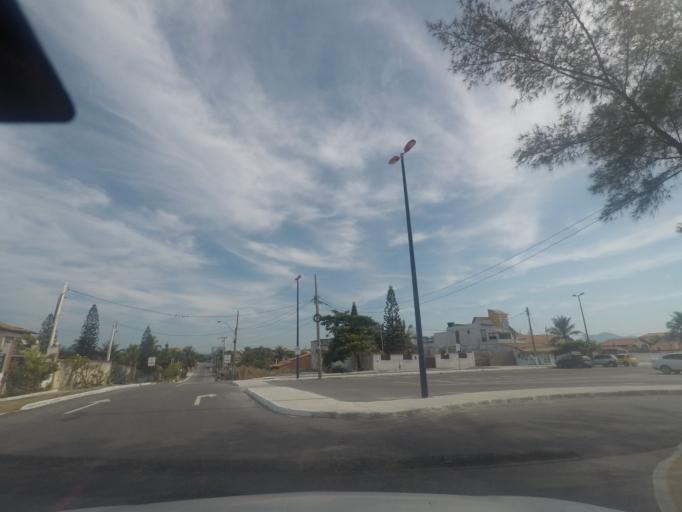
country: BR
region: Rio de Janeiro
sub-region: Marica
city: Marica
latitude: -22.9613
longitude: -42.8228
